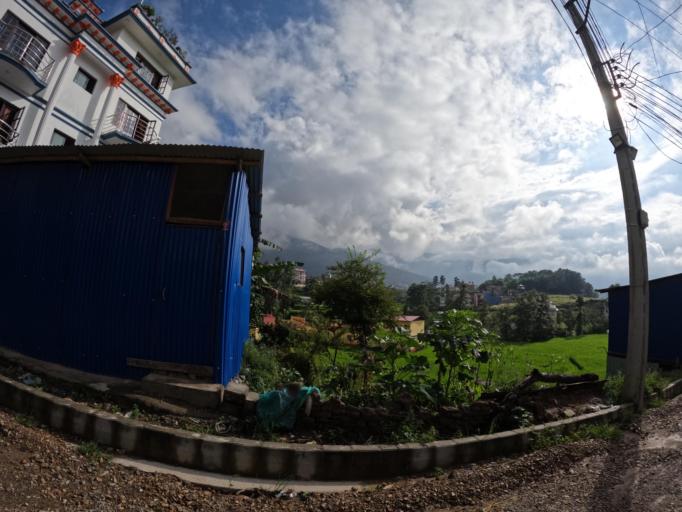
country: NP
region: Central Region
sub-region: Bagmati Zone
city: Kathmandu
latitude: 27.7681
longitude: 85.3315
